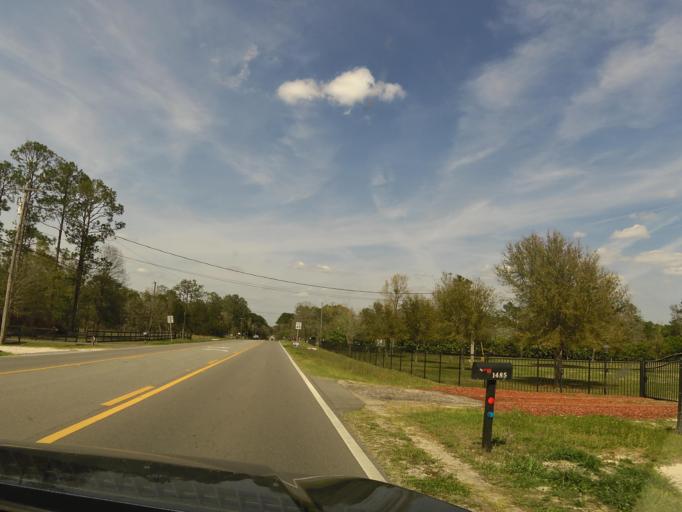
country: US
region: Florida
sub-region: Clay County
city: Middleburg
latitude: 30.1022
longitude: -81.8645
